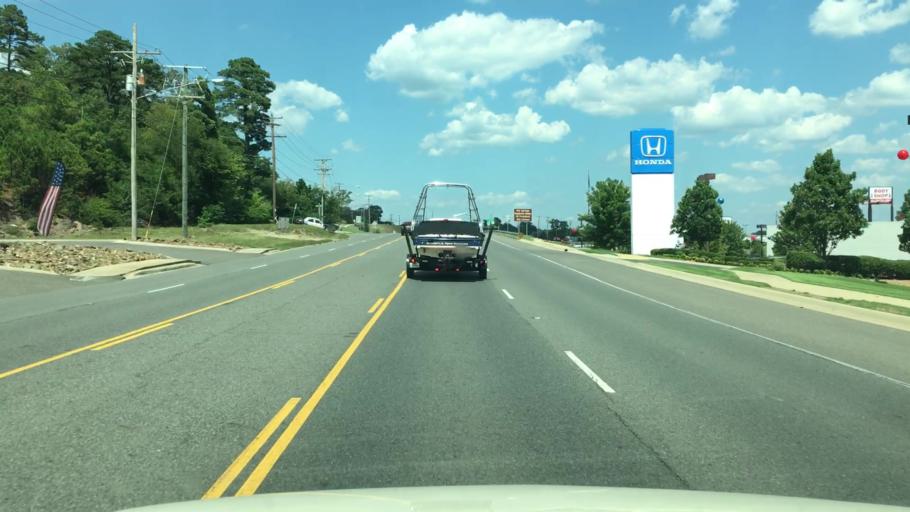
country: US
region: Arkansas
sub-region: Garland County
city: Lake Hamilton
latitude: 34.4469
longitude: -93.0889
